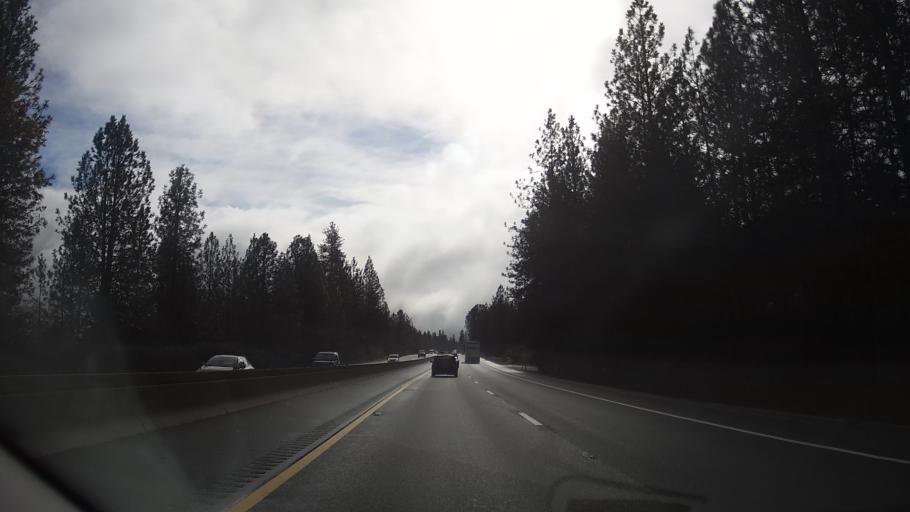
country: US
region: California
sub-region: Placer County
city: Colfax
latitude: 39.0518
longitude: -120.9709
